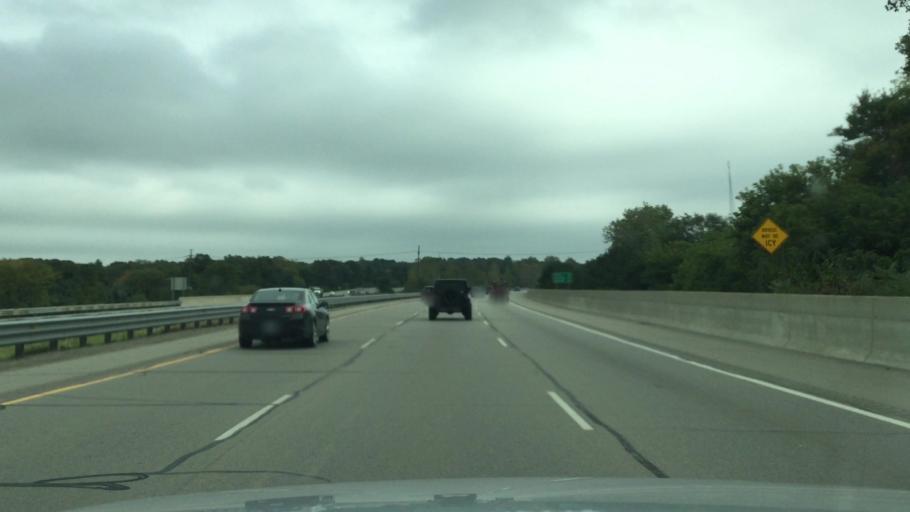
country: US
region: Michigan
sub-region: Oakland County
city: Clarkston
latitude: 42.7454
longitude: -83.4029
